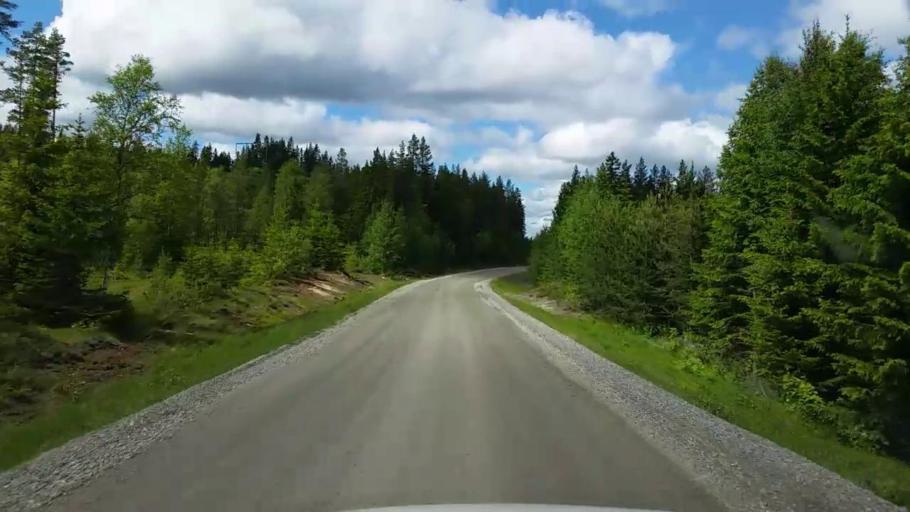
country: SE
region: Gaevleborg
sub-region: Bollnas Kommun
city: Vittsjo
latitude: 61.1738
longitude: 16.1524
